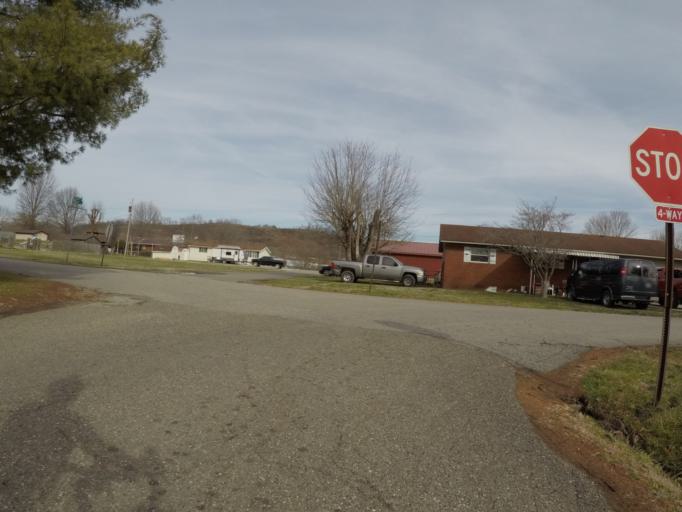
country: US
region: West Virginia
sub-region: Cabell County
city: Huntington
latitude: 38.4399
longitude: -82.3841
